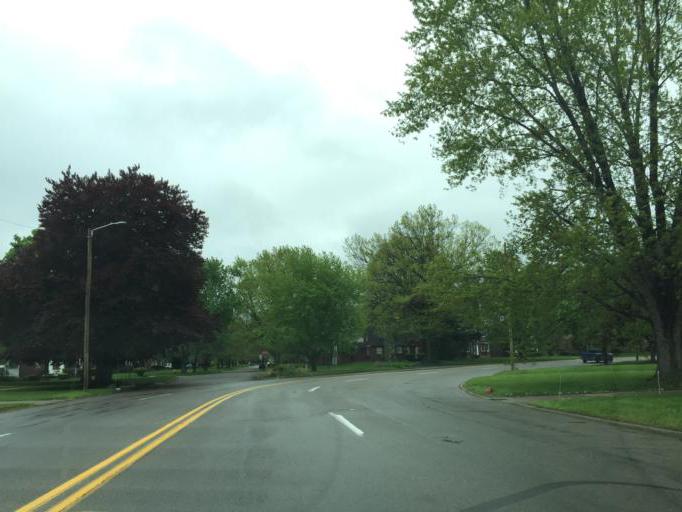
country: US
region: Michigan
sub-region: Wayne County
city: Redford
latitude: 42.3991
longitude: -83.2326
